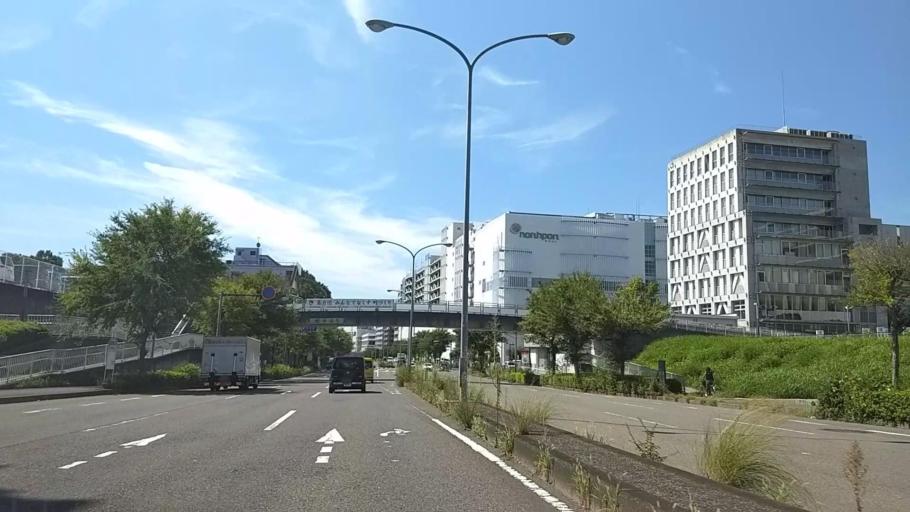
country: JP
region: Tokyo
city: Chofugaoka
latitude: 35.5540
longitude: 139.5813
